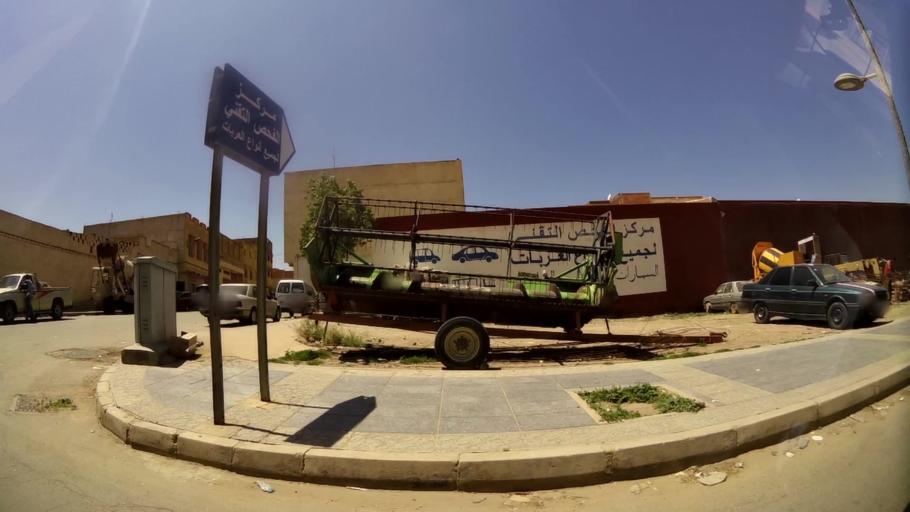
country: MA
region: Oriental
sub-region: Oujda-Angad
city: Oujda
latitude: 34.6860
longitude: -1.9536
